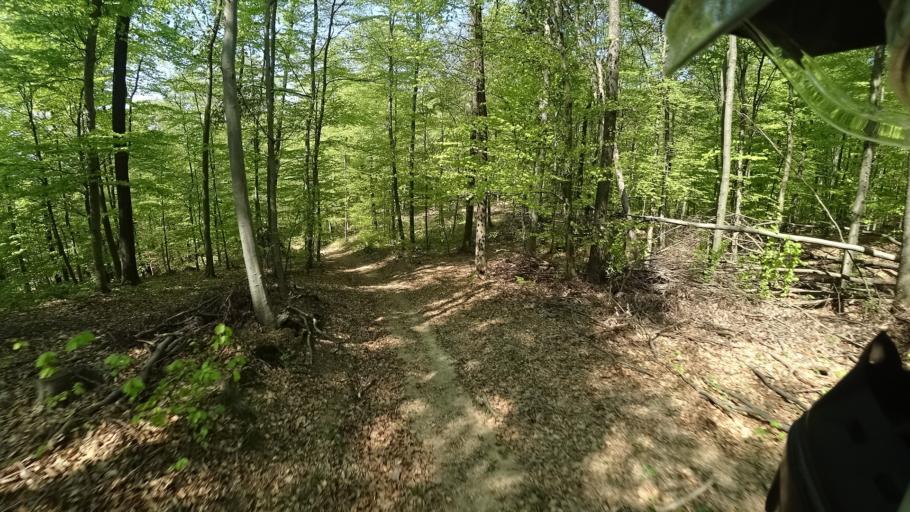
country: HR
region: Zagrebacka
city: Jablanovec
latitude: 45.9101
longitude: 15.9094
